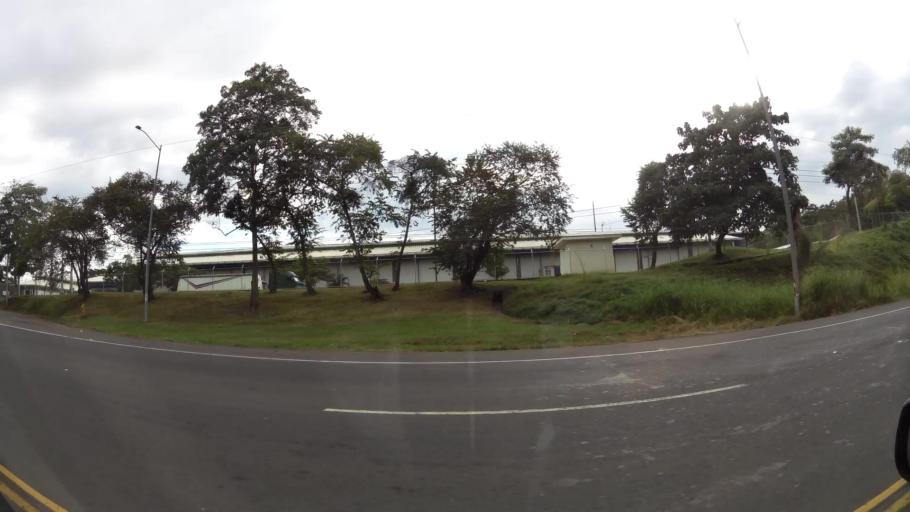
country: CR
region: Puntarenas
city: Esparza
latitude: 9.9079
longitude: -84.6682
